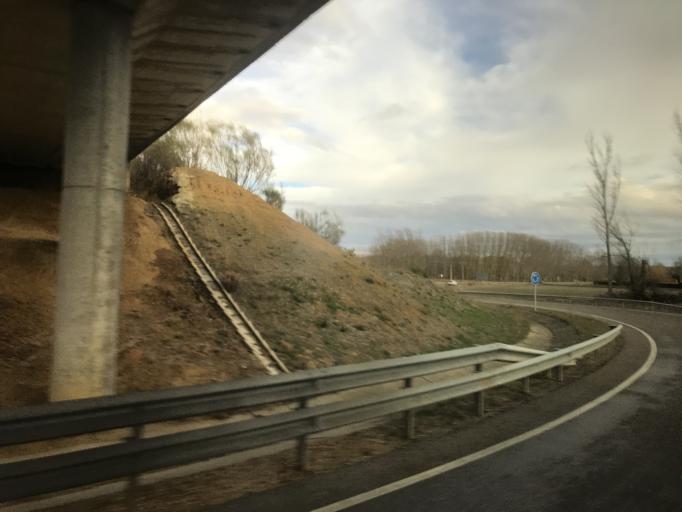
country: ES
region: Castille and Leon
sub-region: Provincia de Palencia
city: Grijota
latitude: 42.0387
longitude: -4.5653
